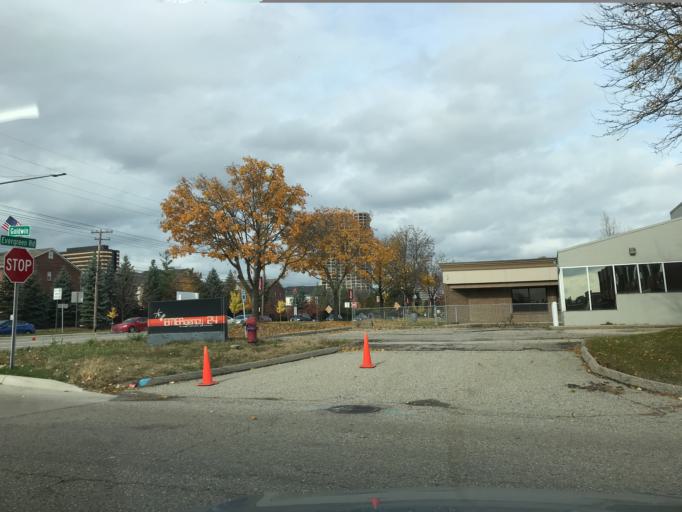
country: US
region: Michigan
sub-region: Oakland County
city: Southfield
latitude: 42.4756
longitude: -83.2402
